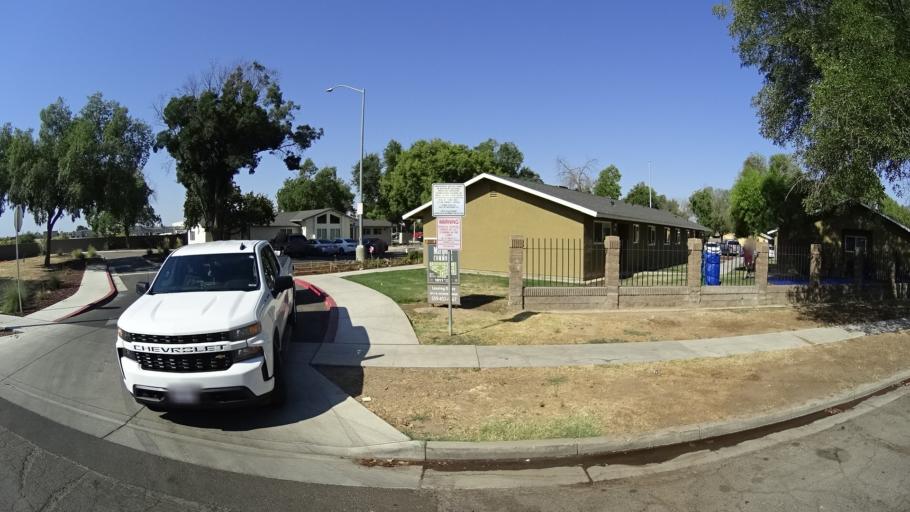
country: US
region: California
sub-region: Fresno County
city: West Park
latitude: 36.7204
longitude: -119.8232
